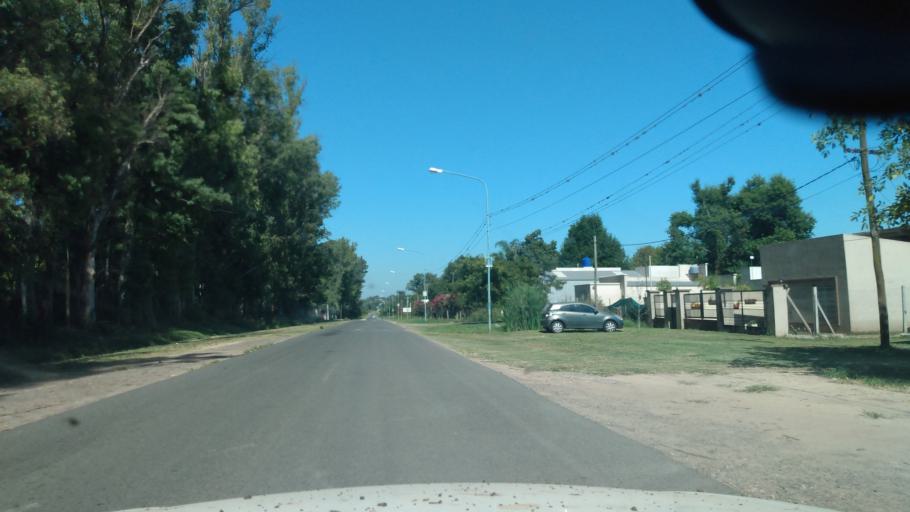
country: AR
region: Buenos Aires
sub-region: Partido de Lujan
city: Lujan
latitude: -34.5052
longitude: -59.0776
